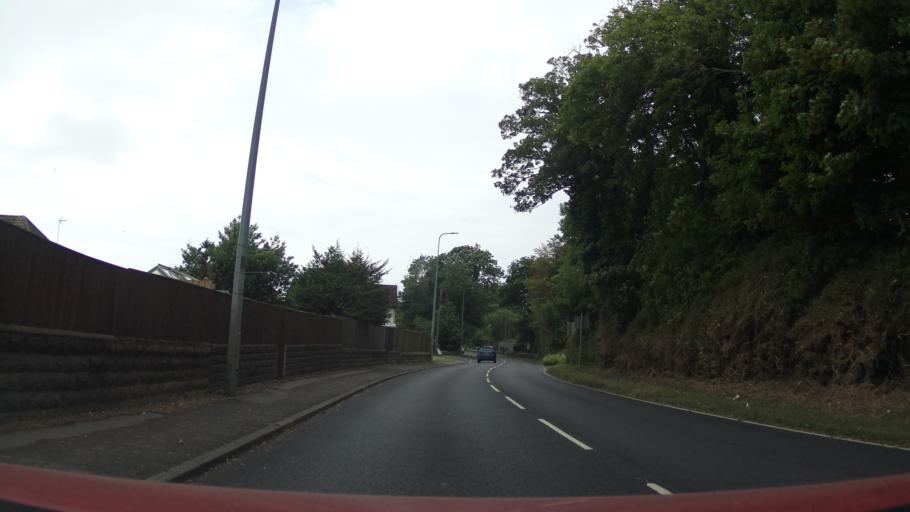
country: GB
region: Wales
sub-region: Vale of Glamorgan
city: Penarth
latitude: 51.4221
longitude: -3.1766
